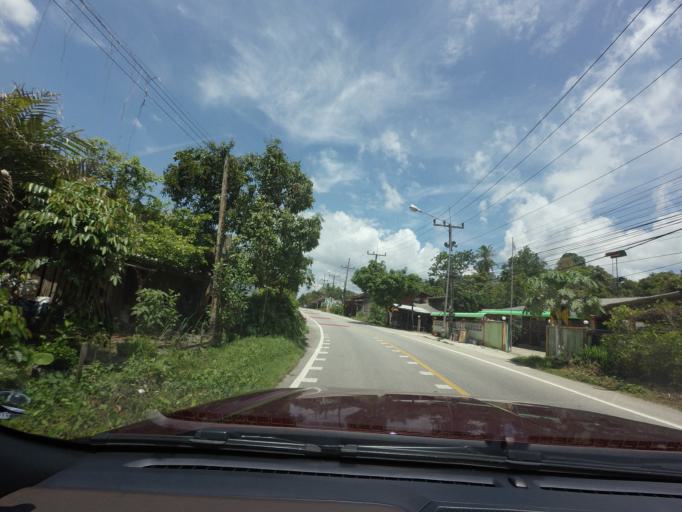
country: TH
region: Narathiwat
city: Ra-ngae
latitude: 6.2387
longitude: 101.6773
